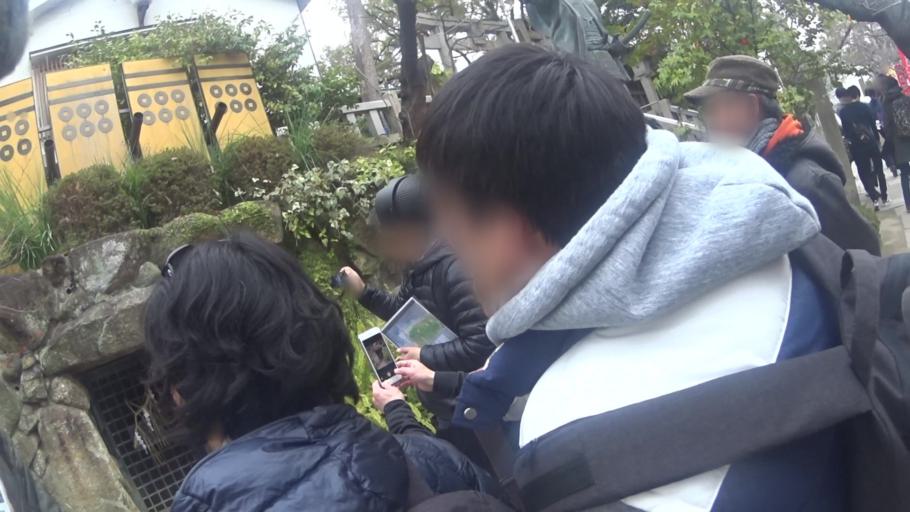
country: JP
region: Osaka
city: Osaka-shi
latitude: 34.6734
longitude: 135.5293
